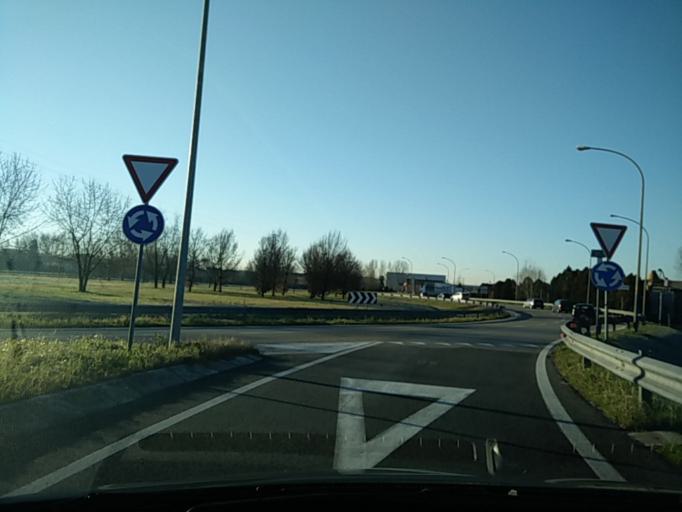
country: IT
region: Veneto
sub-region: Provincia di Venezia
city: Ballo
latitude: 45.4527
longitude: 12.0825
